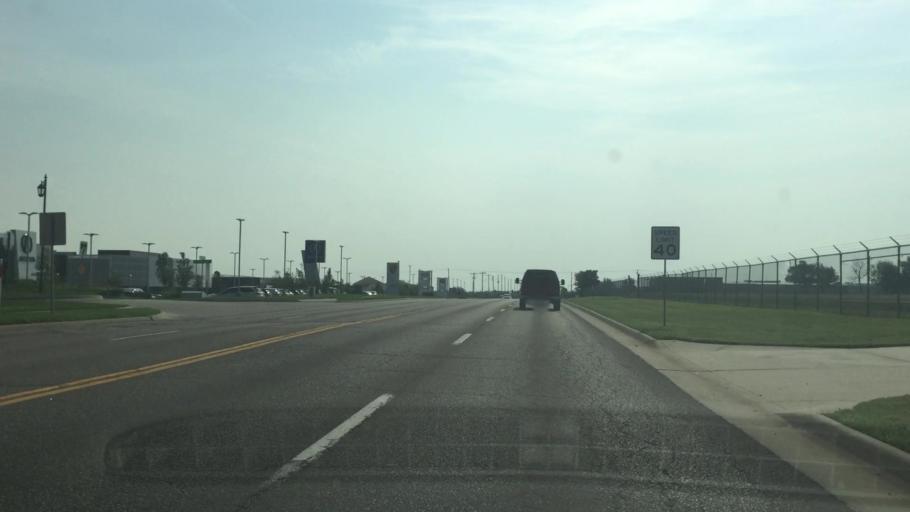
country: US
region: Kansas
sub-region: Butler County
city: Andover
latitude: 37.7085
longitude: -97.2127
